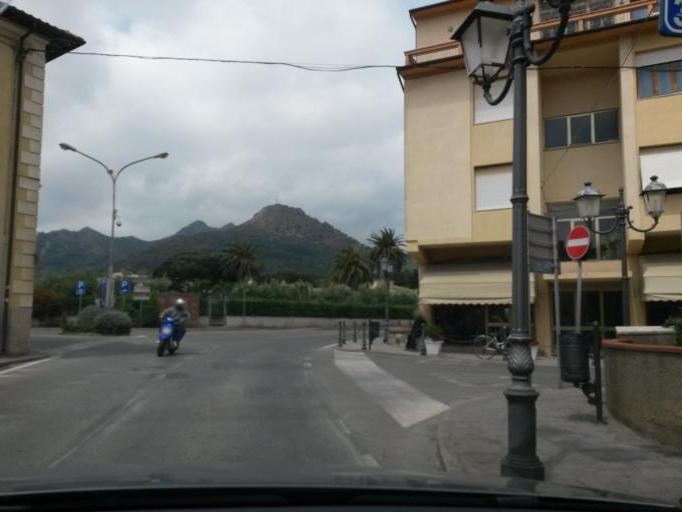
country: IT
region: Tuscany
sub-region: Provincia di Livorno
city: Porto Azzurro
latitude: 42.7672
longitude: 10.3948
